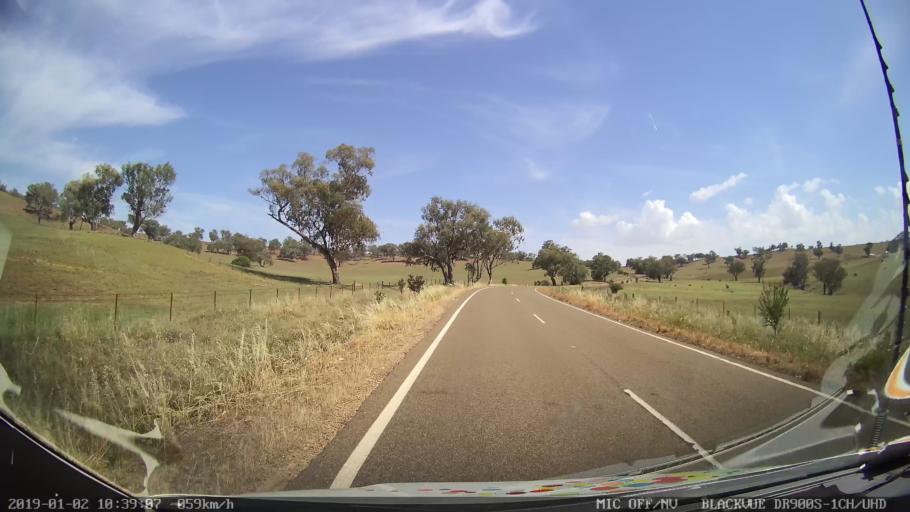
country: AU
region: New South Wales
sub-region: Gundagai
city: Gundagai
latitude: -34.8136
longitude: 148.3200
